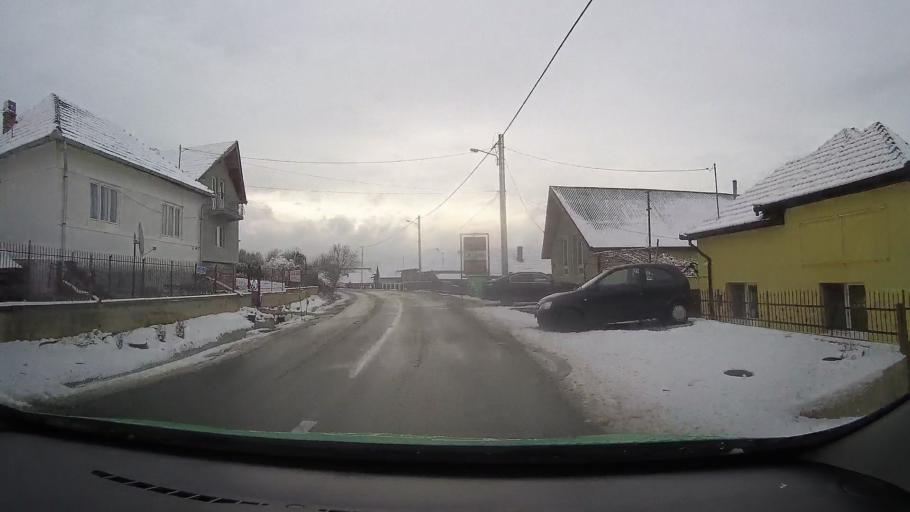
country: RO
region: Hunedoara
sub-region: Oras Hateg
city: Hateg
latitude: 45.6313
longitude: 22.9296
